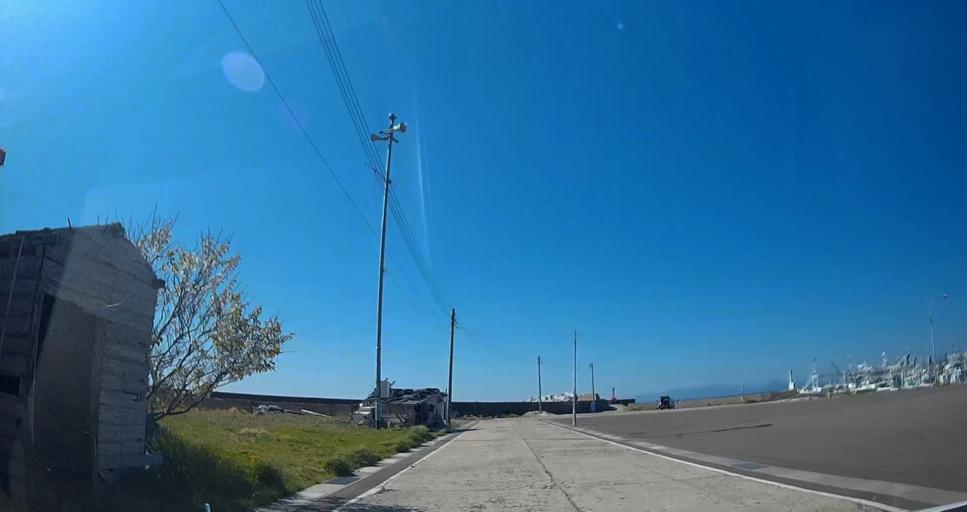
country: JP
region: Hokkaido
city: Hakodate
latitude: 41.5290
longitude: 140.9048
